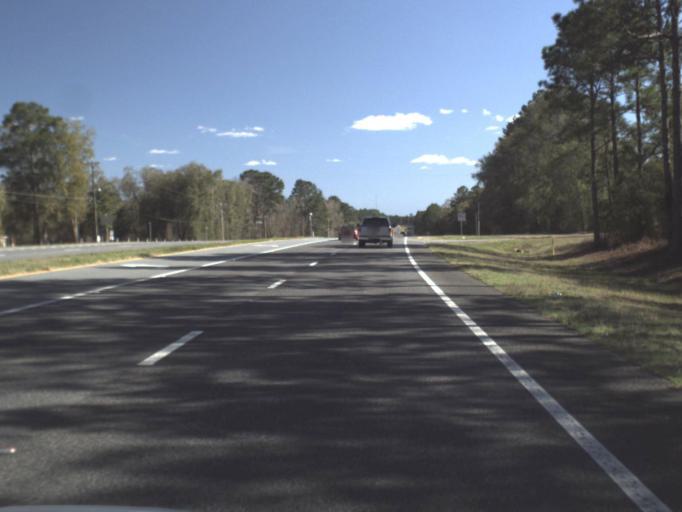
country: US
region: Florida
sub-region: Gadsden County
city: Midway
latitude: 30.5363
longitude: -84.4762
